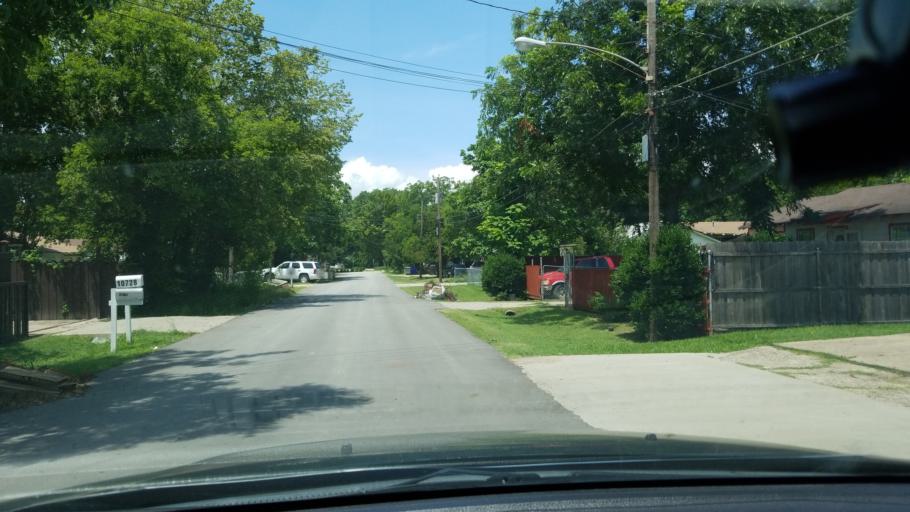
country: US
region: Texas
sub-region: Dallas County
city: Balch Springs
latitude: 32.7452
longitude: -96.6410
